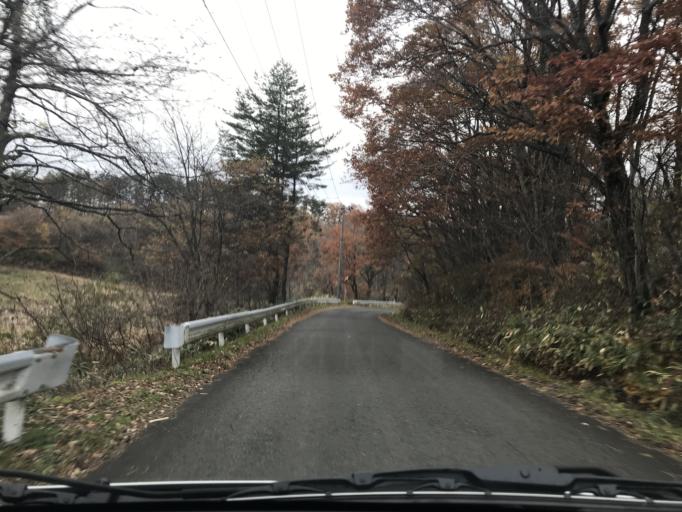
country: JP
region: Iwate
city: Ichinoseki
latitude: 38.9887
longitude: 141.0123
